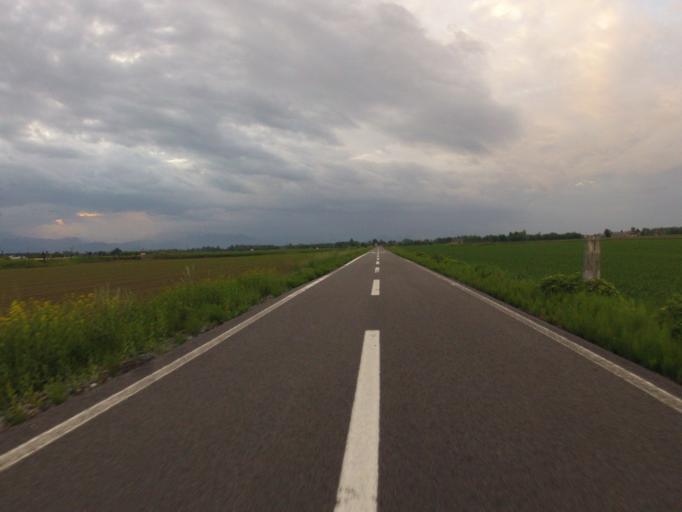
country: IT
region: Piedmont
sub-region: Provincia di Torino
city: Villafranca Piemonte
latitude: 44.7978
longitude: 7.5055
